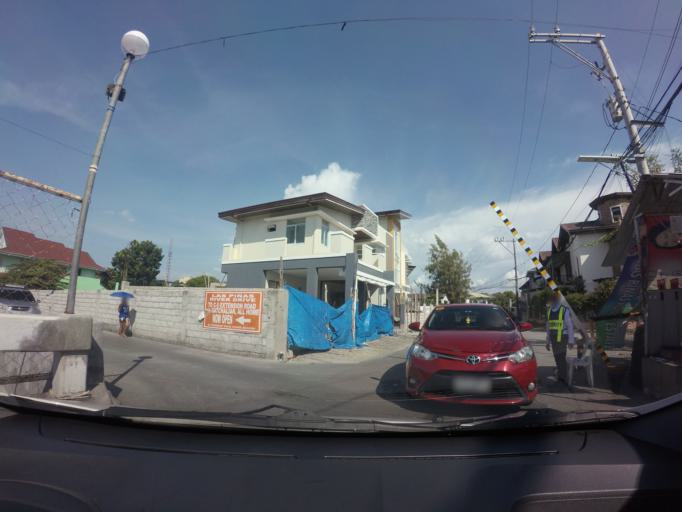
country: PH
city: Sambayanihan People's Village
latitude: 14.4698
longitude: 120.9859
